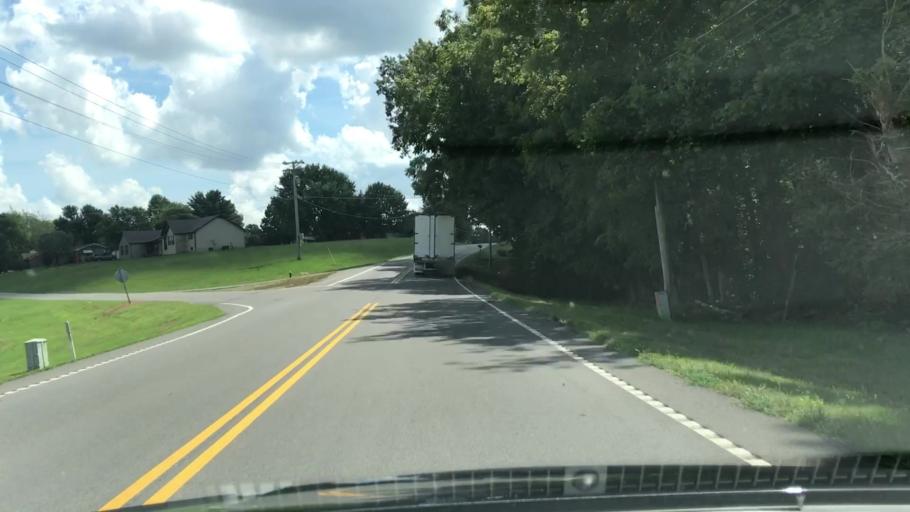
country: US
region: Tennessee
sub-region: Robertson County
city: Cross Plains
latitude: 36.5452
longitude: -86.6826
